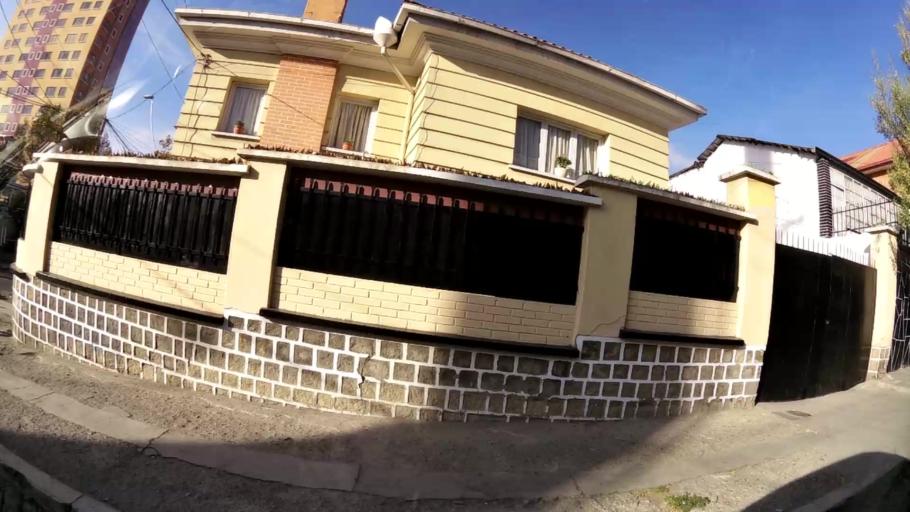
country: BO
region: La Paz
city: La Paz
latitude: -16.4883
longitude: -68.1218
